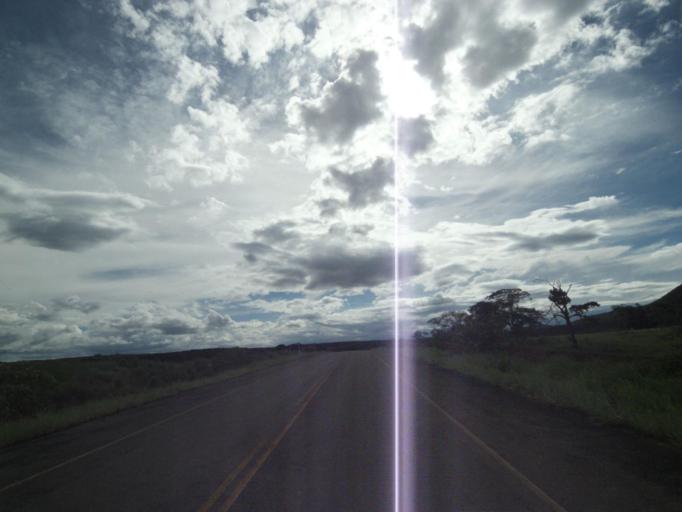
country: BR
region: Goias
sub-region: Jaragua
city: Jaragua
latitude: -15.8382
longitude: -49.2821
